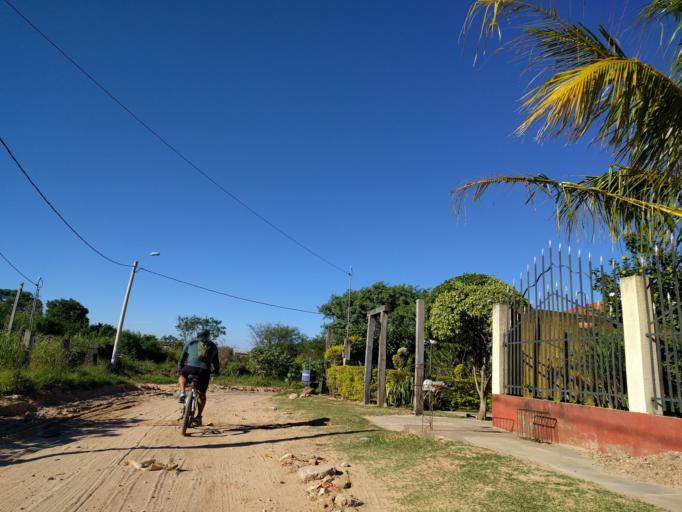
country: BO
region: Santa Cruz
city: Santa Cruz de la Sierra
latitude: -17.8473
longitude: -63.2391
